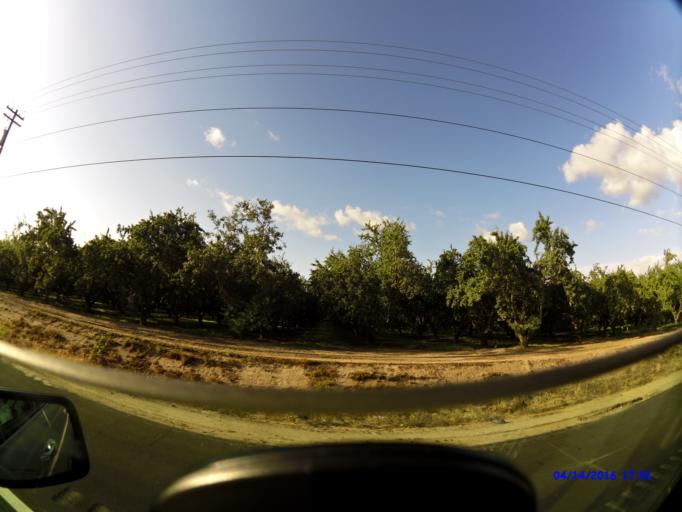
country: US
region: California
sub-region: Stanislaus County
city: Riverbank
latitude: 37.7111
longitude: -120.9729
